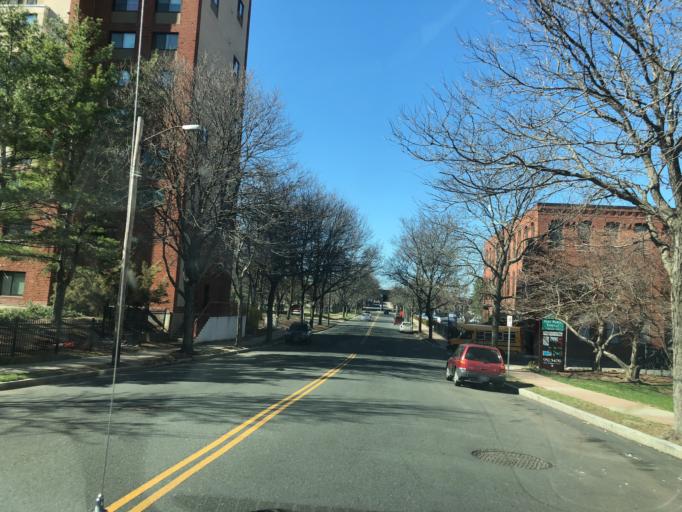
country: US
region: Connecticut
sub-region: Hartford County
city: Hartford
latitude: 41.7591
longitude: -72.6968
